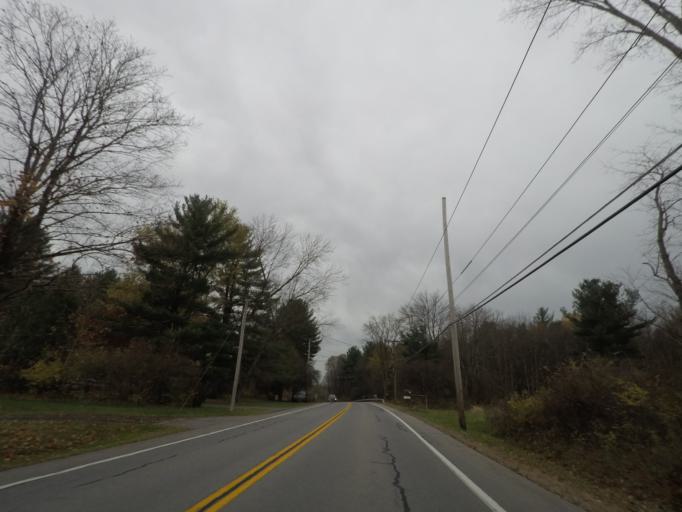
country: US
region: New York
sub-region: Schenectady County
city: Niskayuna
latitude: 42.8080
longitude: -73.8257
